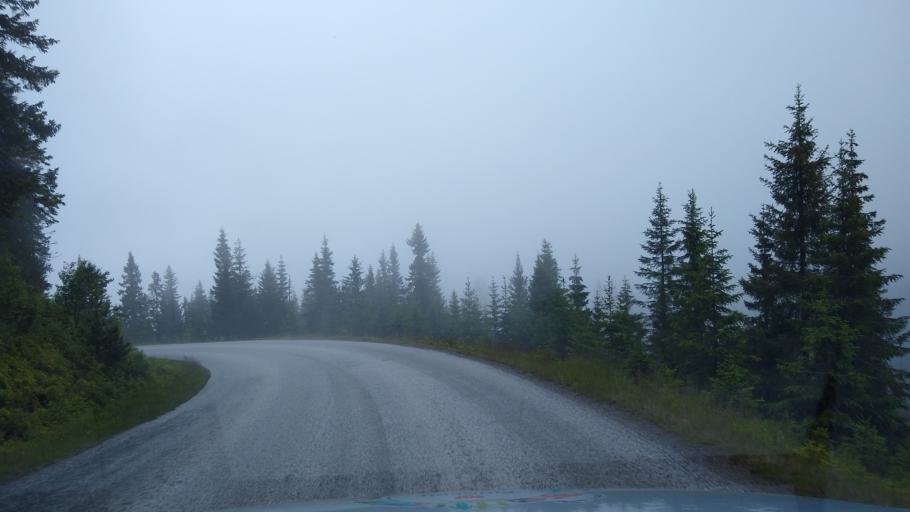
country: NO
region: Oppland
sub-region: Ringebu
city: Ringebu
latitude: 61.4915
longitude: 10.1330
